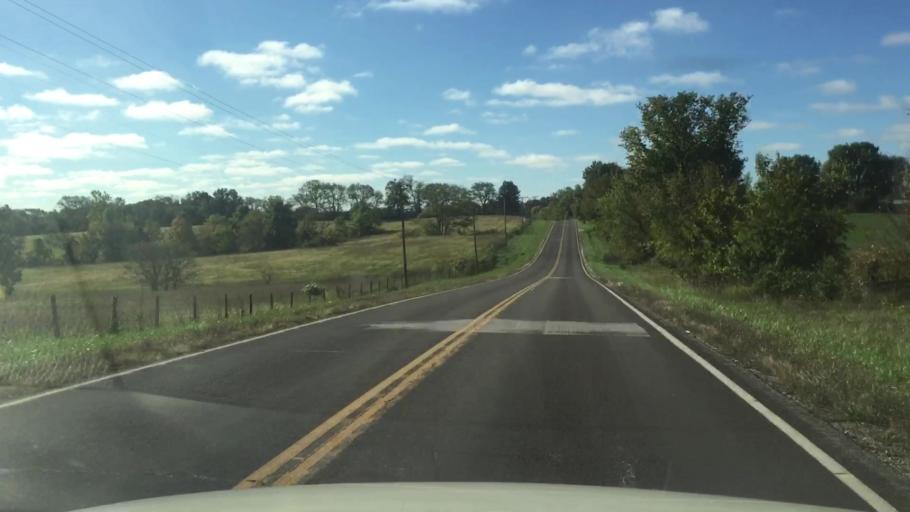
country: US
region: Missouri
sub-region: Howard County
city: New Franklin
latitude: 39.0424
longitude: -92.7445
